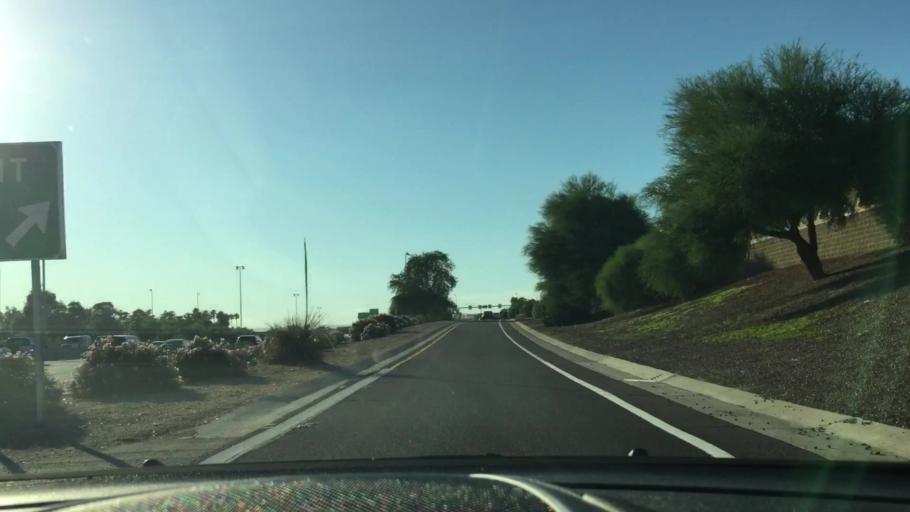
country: US
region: Arizona
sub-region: Maricopa County
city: Sun City
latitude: 33.6681
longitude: -112.2161
